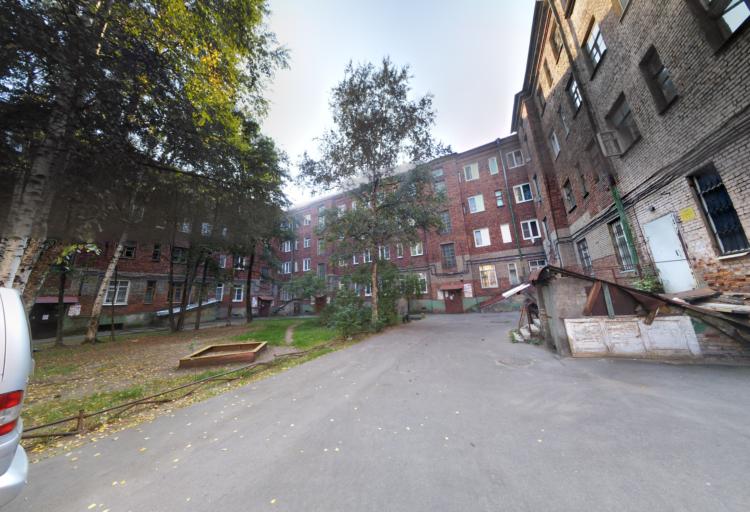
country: RU
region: Jaroslavl
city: Yaroslavl
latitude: 57.6286
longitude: 39.8769
